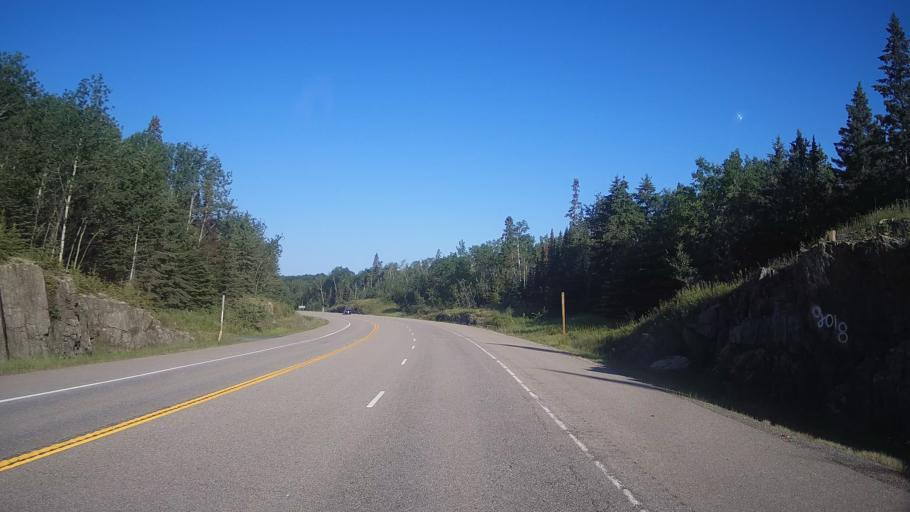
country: US
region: Minnesota
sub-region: Roseau County
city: Warroad
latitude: 49.7187
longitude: -94.7265
